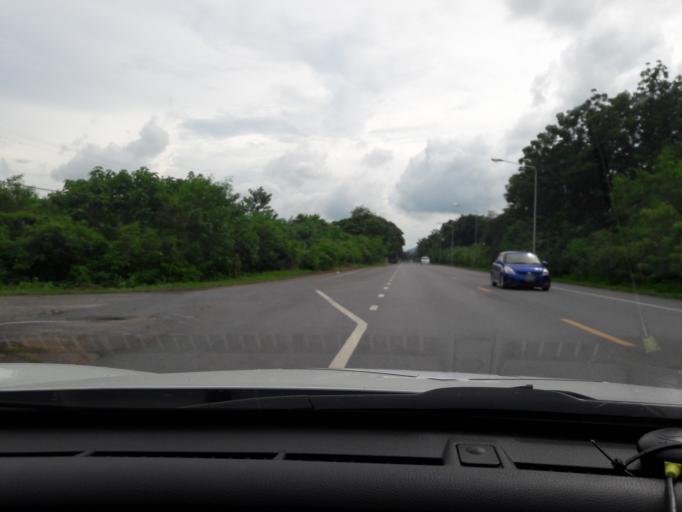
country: TH
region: Nakhon Sawan
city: Tak Fa
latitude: 15.3659
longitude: 100.5058
